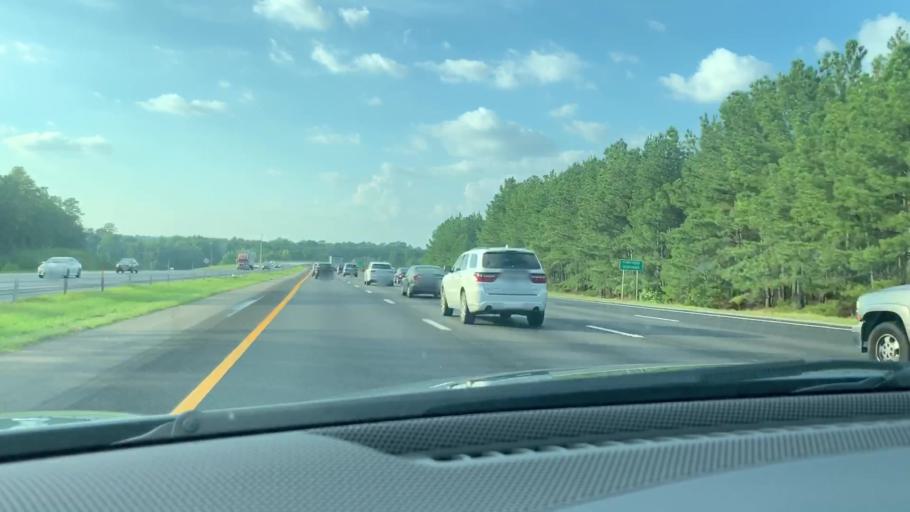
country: US
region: South Carolina
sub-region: Richland County
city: Forest Acres
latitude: 33.9920
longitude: -80.9544
